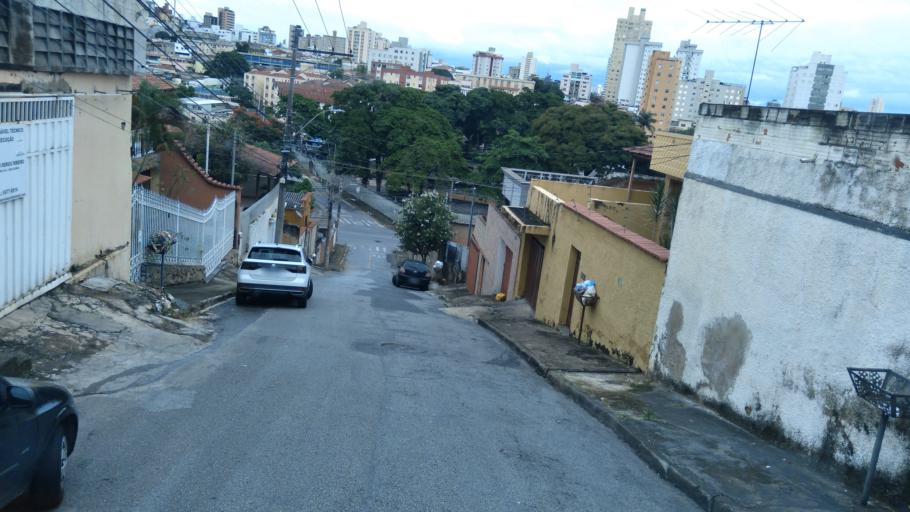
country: BR
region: Minas Gerais
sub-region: Belo Horizonte
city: Belo Horizonte
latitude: -19.9225
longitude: -43.9104
